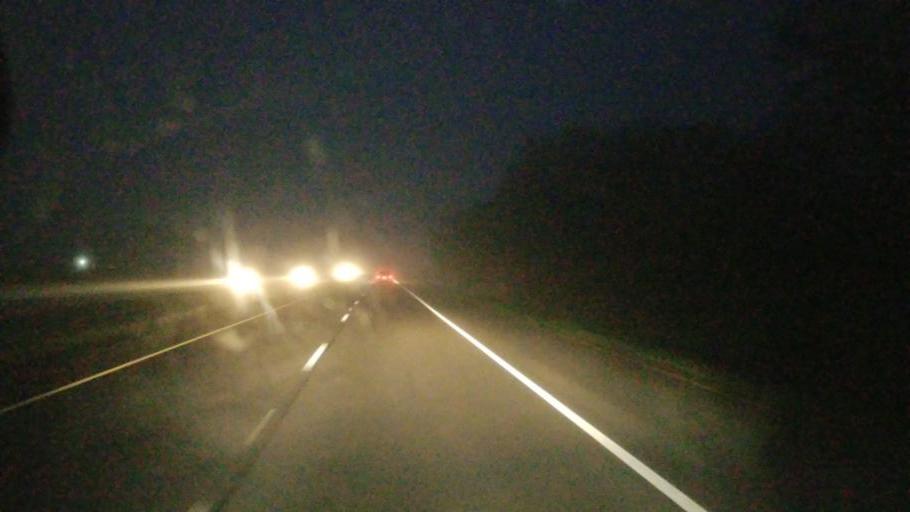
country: US
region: Ohio
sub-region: Ross County
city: Kingston
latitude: 39.4603
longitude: -82.9704
